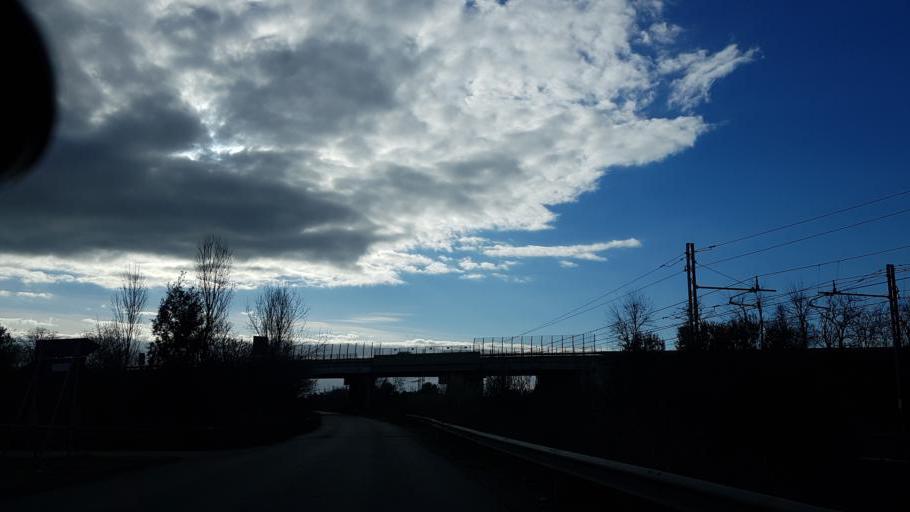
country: IT
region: Apulia
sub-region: Provincia di Brindisi
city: La Rosa
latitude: 40.6188
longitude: 17.9510
